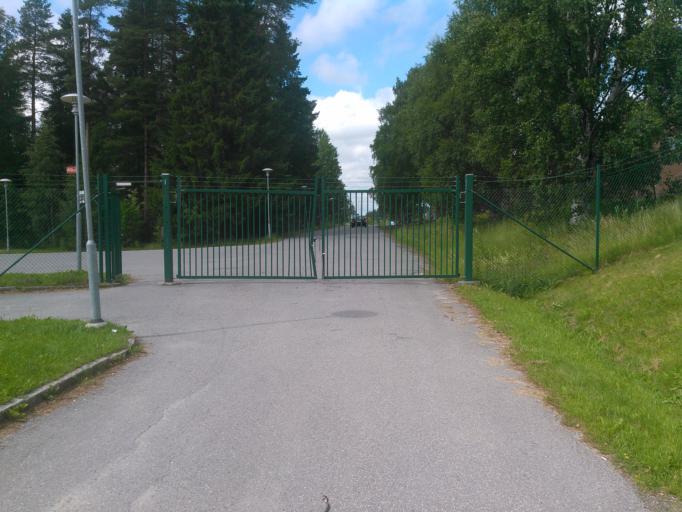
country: SE
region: Vaesterbotten
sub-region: Umea Kommun
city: Umea
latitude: 63.8354
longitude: 20.2566
